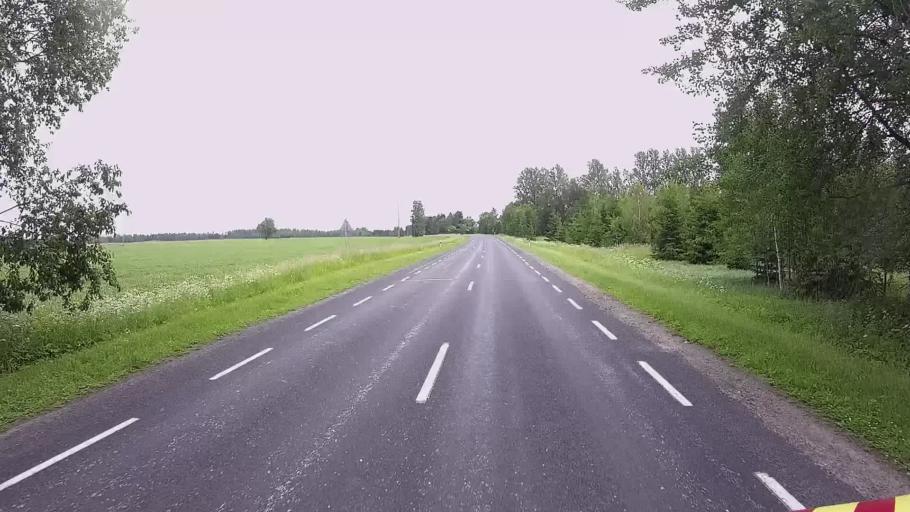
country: EE
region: Viljandimaa
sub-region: Karksi vald
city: Karksi-Nuia
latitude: 58.1946
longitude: 25.6115
